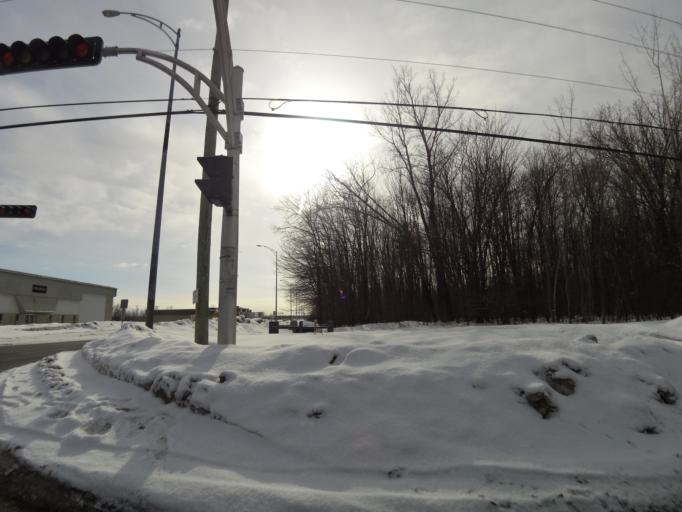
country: CA
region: Quebec
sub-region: Outaouais
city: Gatineau
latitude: 45.5114
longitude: -75.5622
